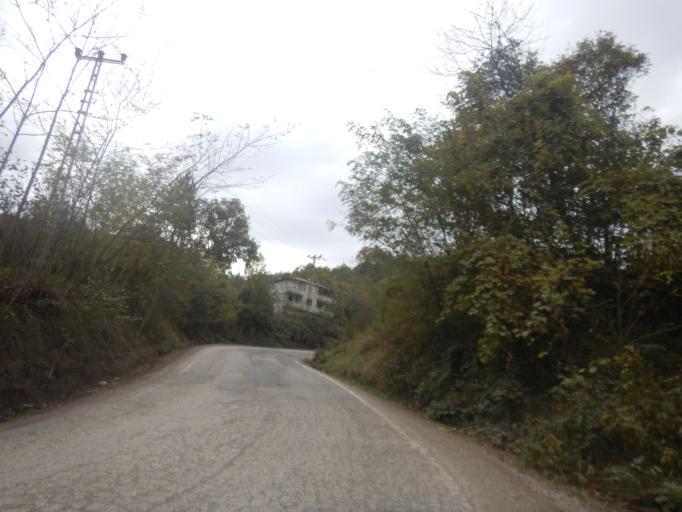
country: TR
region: Ordu
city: Golkoy
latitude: 40.6823
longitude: 37.5662
